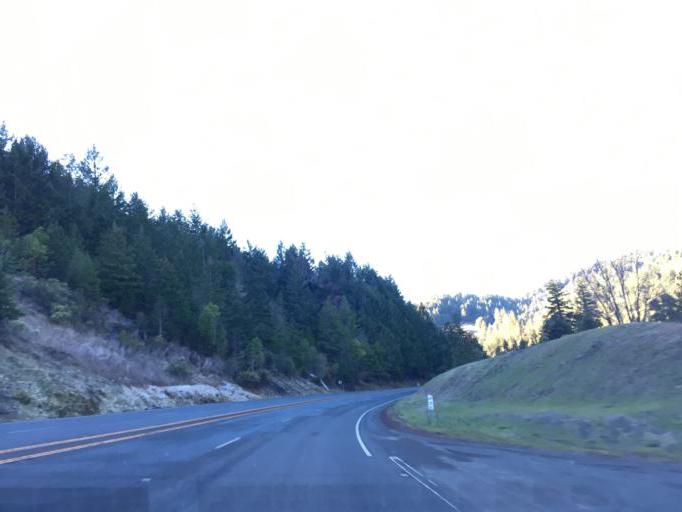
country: US
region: California
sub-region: Mendocino County
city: Laytonville
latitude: 39.8261
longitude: -123.5944
